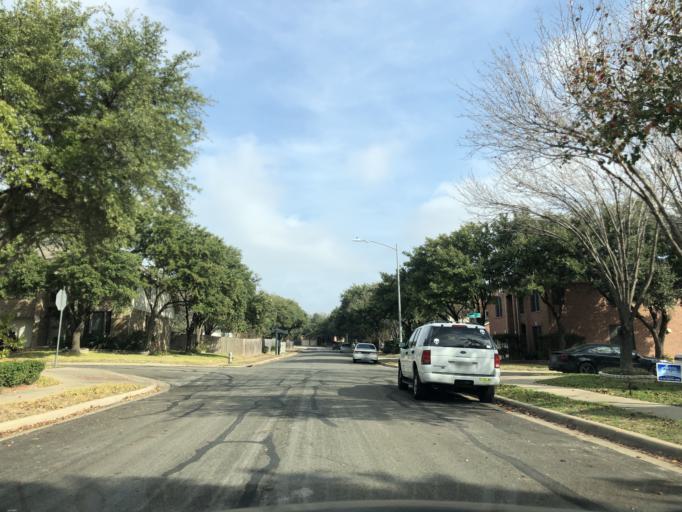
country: US
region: Texas
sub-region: Travis County
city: Wells Branch
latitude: 30.4199
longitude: -97.6807
